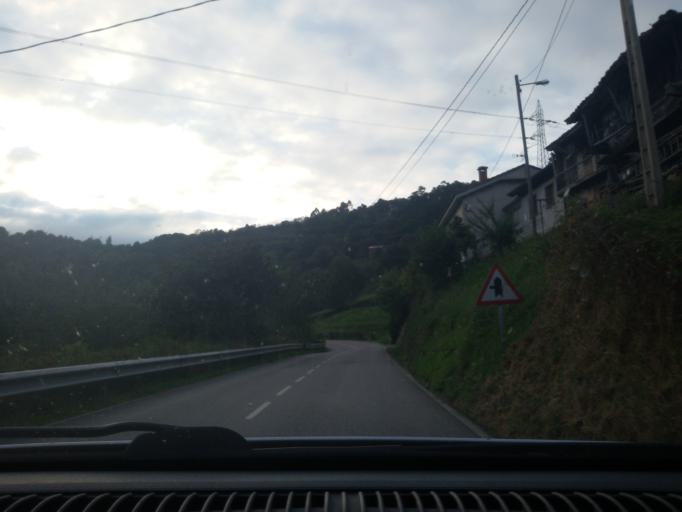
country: ES
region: Asturias
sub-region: Province of Asturias
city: Bimenes
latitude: 43.3337
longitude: -5.5888
